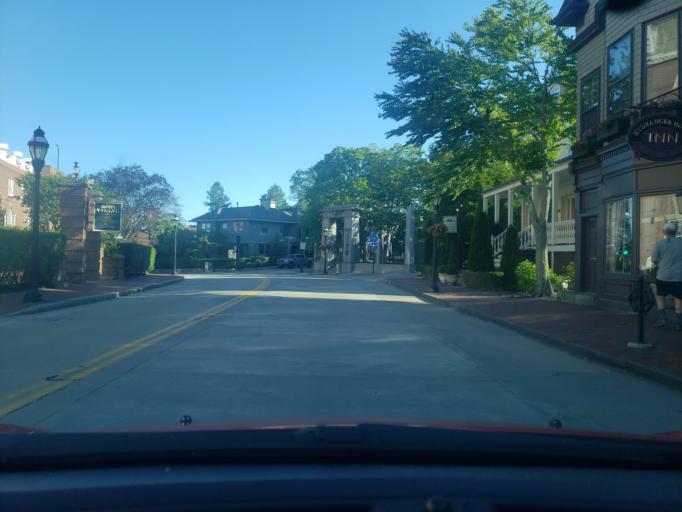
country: US
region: Rhode Island
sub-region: Newport County
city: Newport
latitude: 41.4874
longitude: -71.3094
